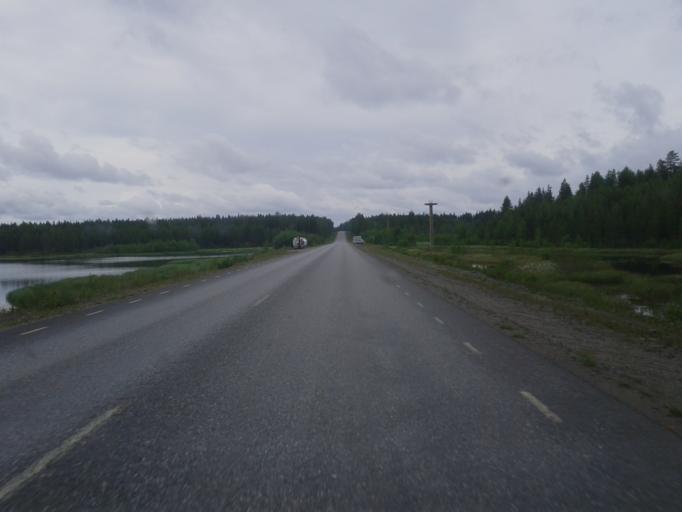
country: SE
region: Vaesterbotten
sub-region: Skelleftea Kommun
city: Langsele
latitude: 64.8845
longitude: 20.2930
